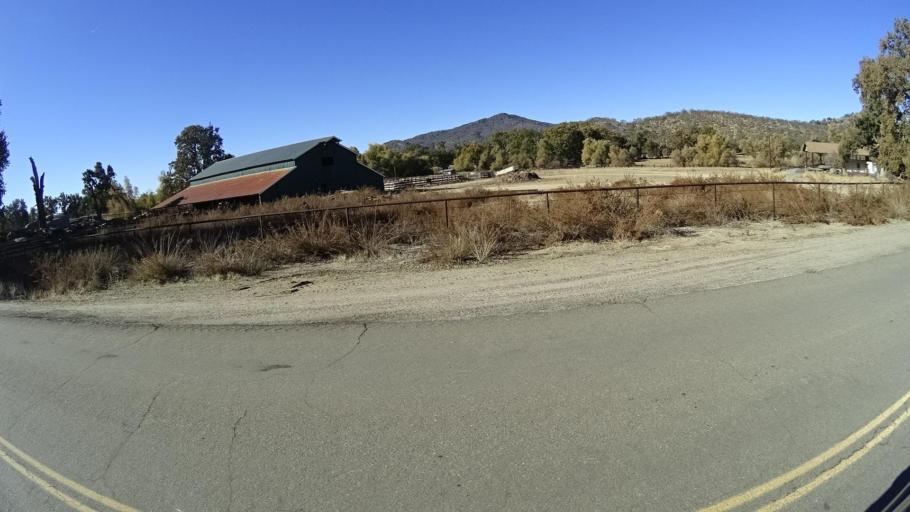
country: US
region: California
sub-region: Kern County
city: Alta Sierra
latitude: 35.7698
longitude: -118.7101
